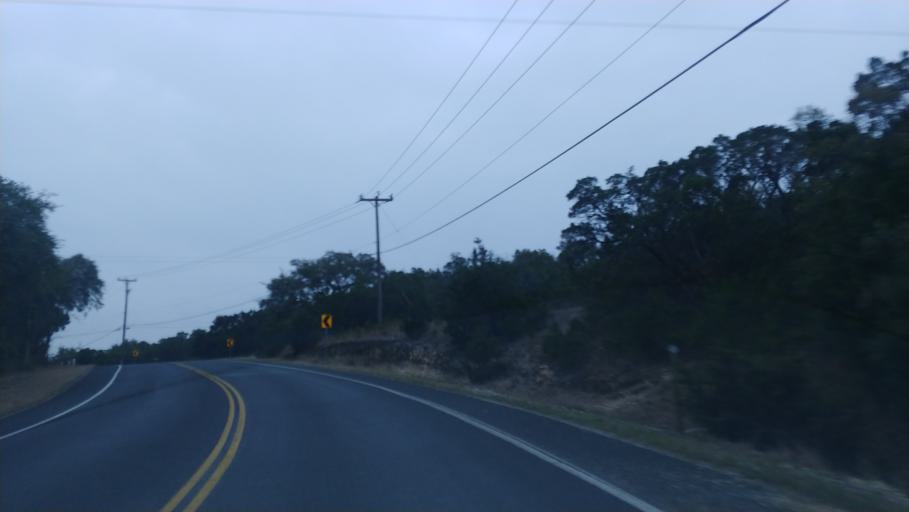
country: US
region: Texas
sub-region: Bexar County
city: Helotes
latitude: 29.5958
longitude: -98.6891
